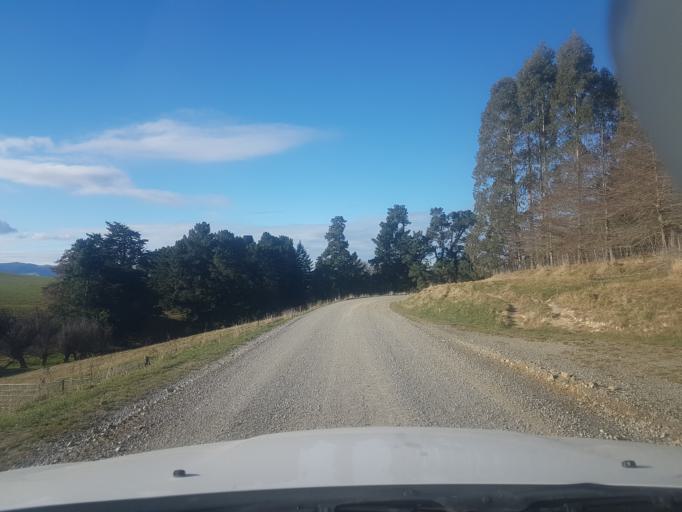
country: NZ
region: Canterbury
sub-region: Timaru District
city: Pleasant Point
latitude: -44.1690
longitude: 170.9198
